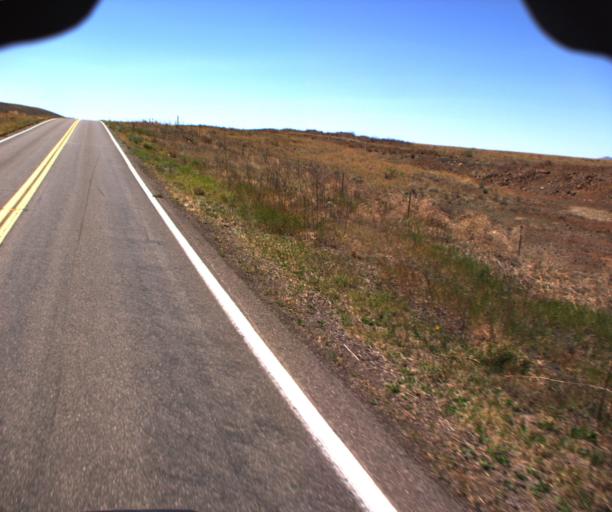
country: US
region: Arizona
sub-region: Cochise County
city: Douglas
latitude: 31.6182
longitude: -109.2148
